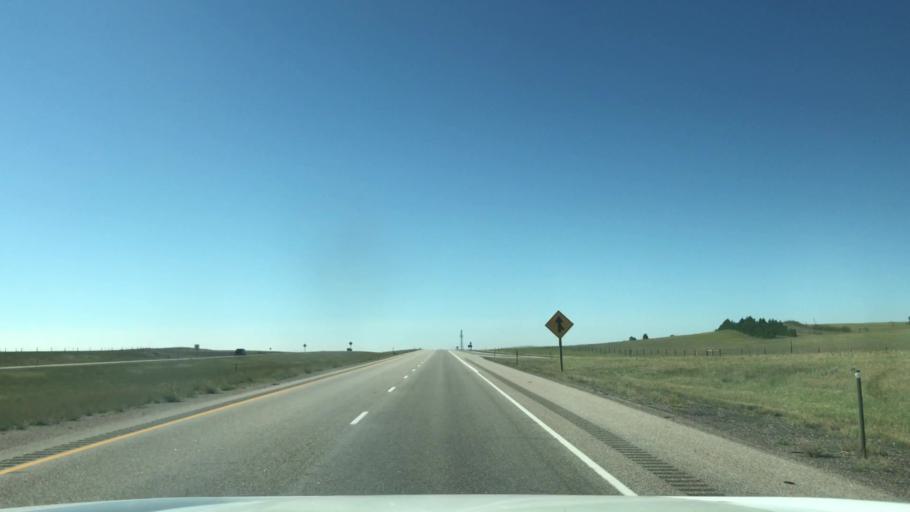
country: US
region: Wyoming
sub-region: Laramie County
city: Ranchettes
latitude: 41.4061
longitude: -104.8745
